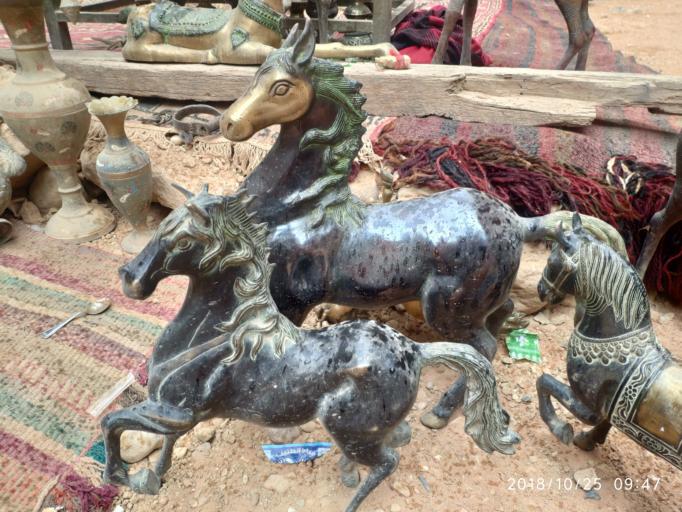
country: JO
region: Ma'an
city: Petra
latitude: 30.3224
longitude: 35.4517
